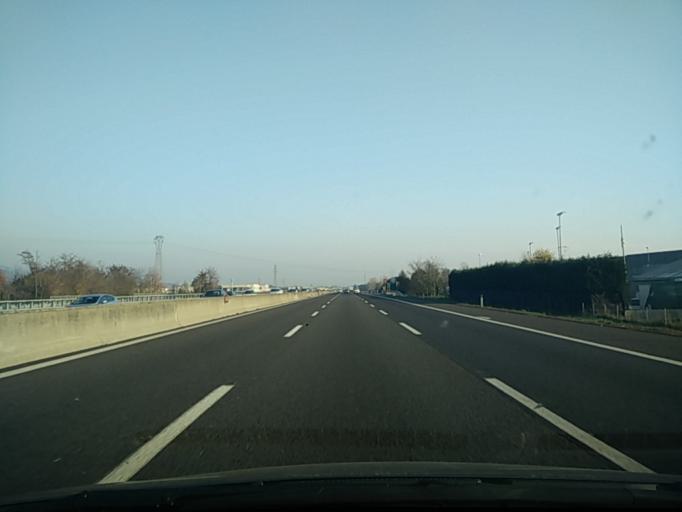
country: IT
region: Lombardy
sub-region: Provincia di Bergamo
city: Bolgare
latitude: 45.6385
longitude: 9.8301
